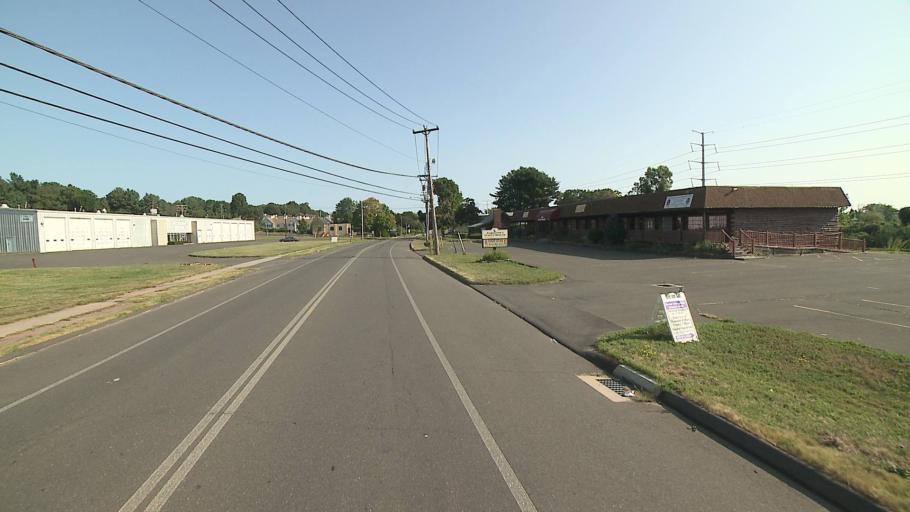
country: US
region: Connecticut
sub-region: New Haven County
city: New Haven
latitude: 41.3429
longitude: -72.8953
